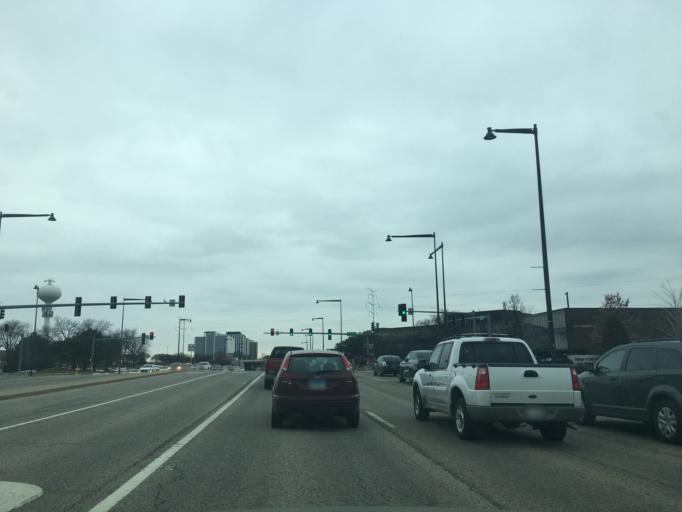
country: US
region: Illinois
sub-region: DuPage County
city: Oak Brook
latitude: 41.8473
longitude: -87.9379
